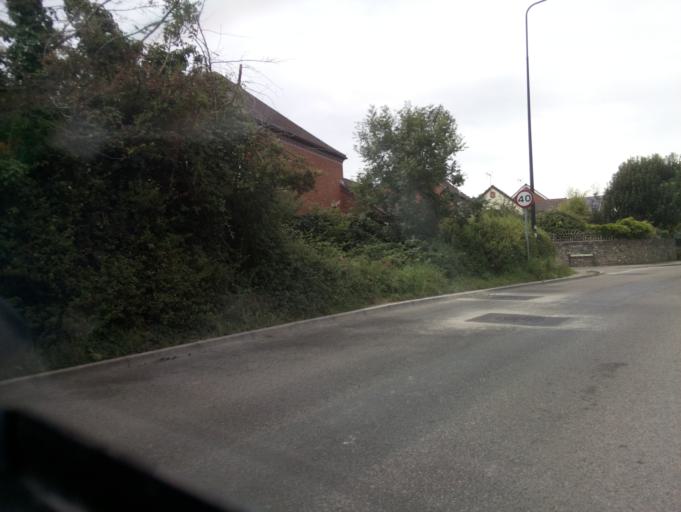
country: GB
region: England
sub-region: North Somerset
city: Yatton
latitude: 51.3945
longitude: -2.8297
